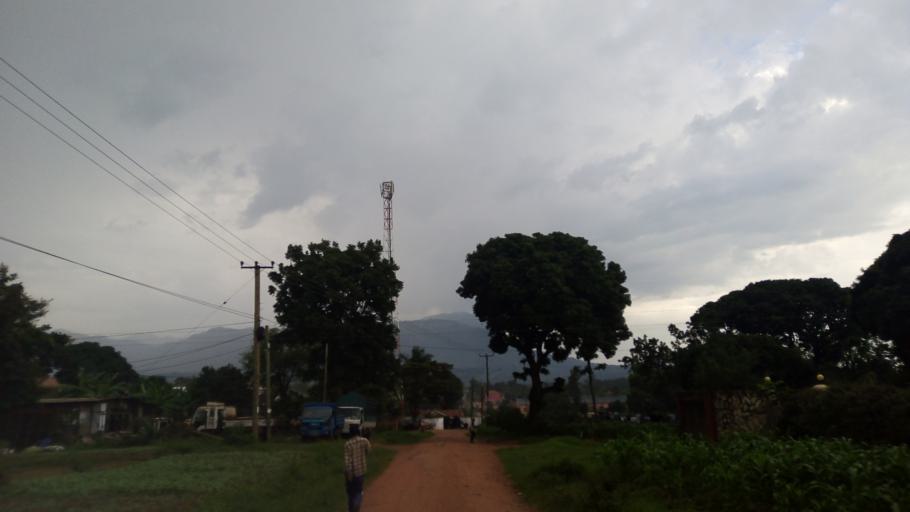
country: UG
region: Eastern Region
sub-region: Mbale District
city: Mbale
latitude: 1.0708
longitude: 34.1733
